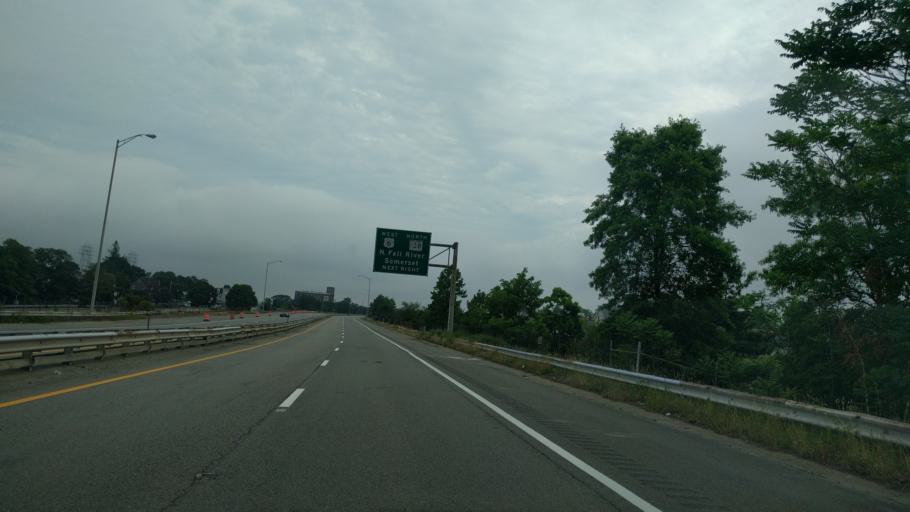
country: US
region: Massachusetts
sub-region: Bristol County
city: Fall River
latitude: 41.7117
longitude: -71.1565
